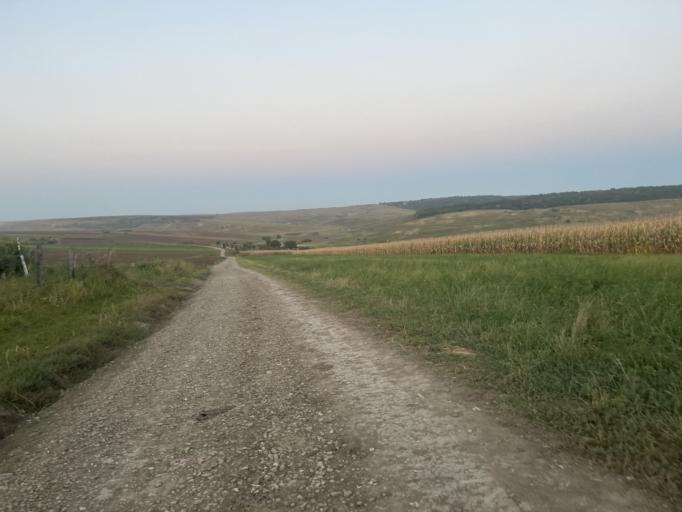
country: RO
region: Iasi
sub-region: Comuna Dumesti
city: Pausesti
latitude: 47.1519
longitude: 27.3281
